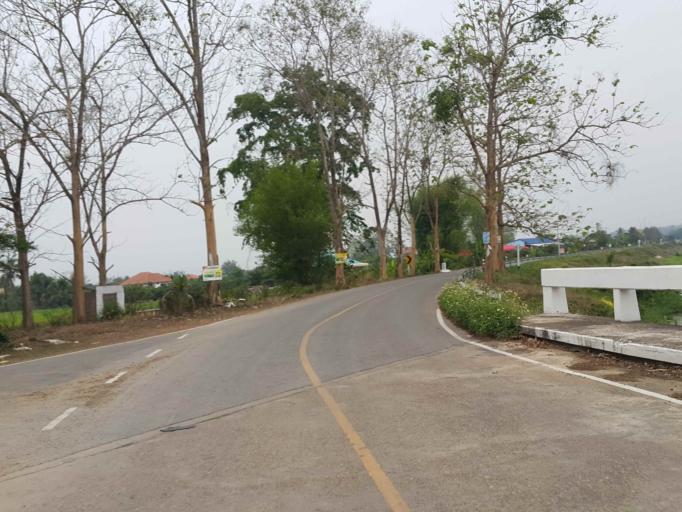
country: TH
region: Chiang Mai
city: Mae Taeng
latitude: 19.0445
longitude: 98.9771
